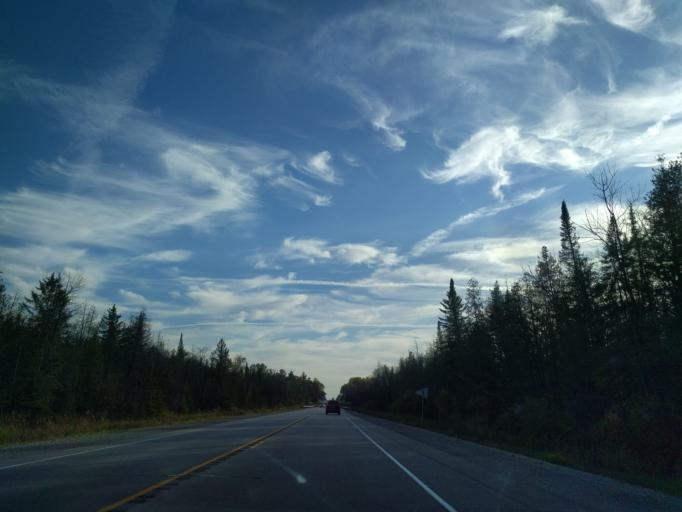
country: US
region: Wisconsin
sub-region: Marinette County
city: Peshtigo
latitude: 45.2581
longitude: -87.9909
